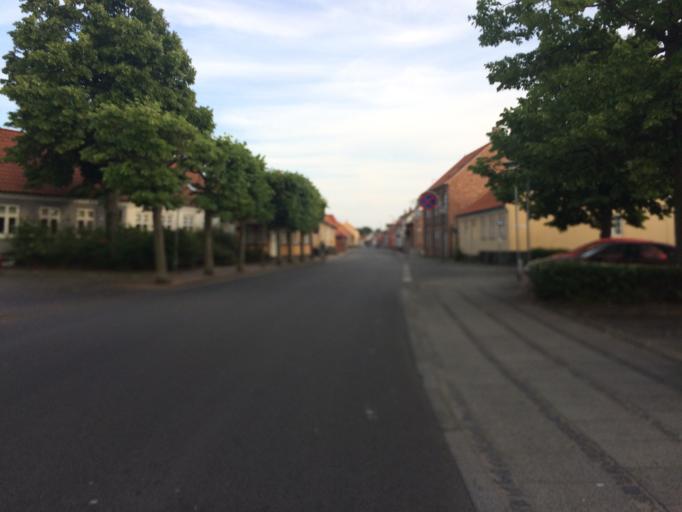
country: DK
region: Capital Region
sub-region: Bornholm Kommune
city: Ronne
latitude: 55.0990
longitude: 14.7015
